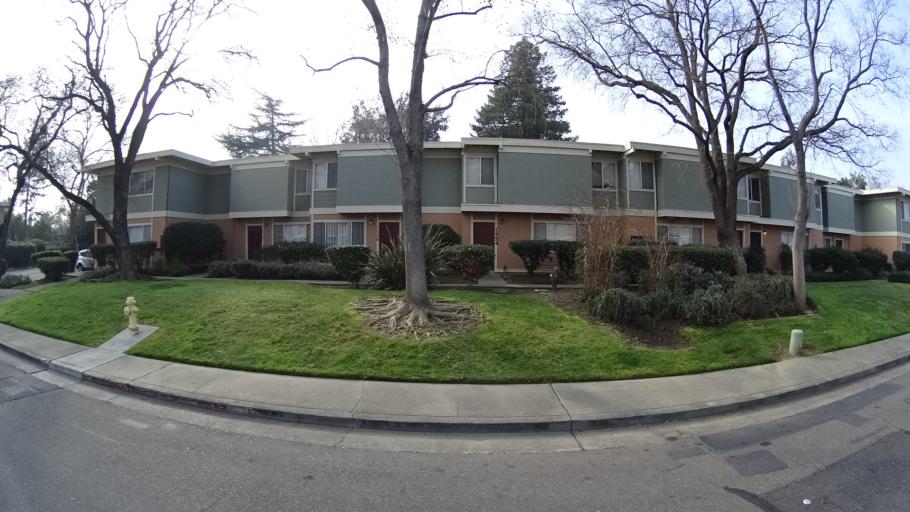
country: US
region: California
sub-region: Yolo County
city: Davis
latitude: 38.5594
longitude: -121.7661
